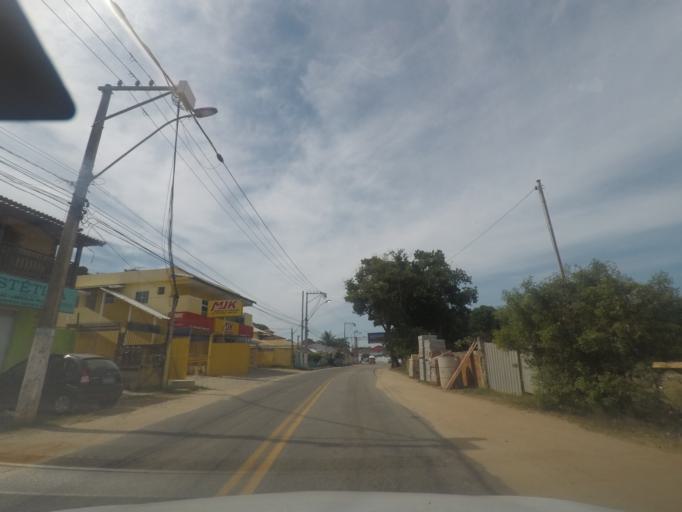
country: BR
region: Rio de Janeiro
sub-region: Marica
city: Marica
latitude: -22.9490
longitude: -42.6974
